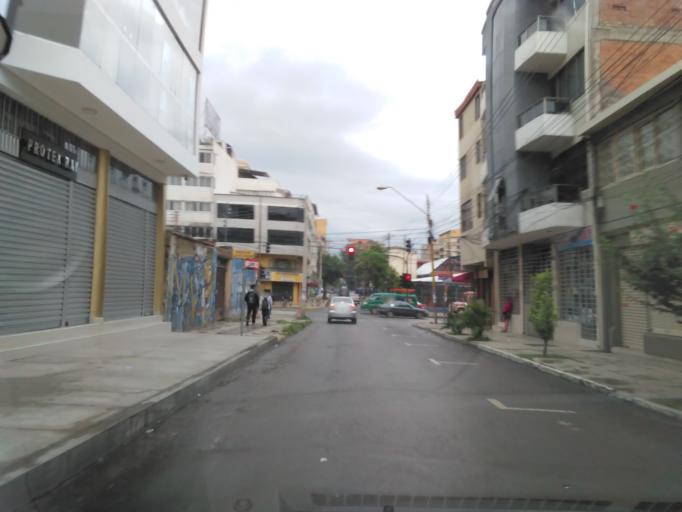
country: BO
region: Cochabamba
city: Cochabamba
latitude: -17.3907
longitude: -66.1513
